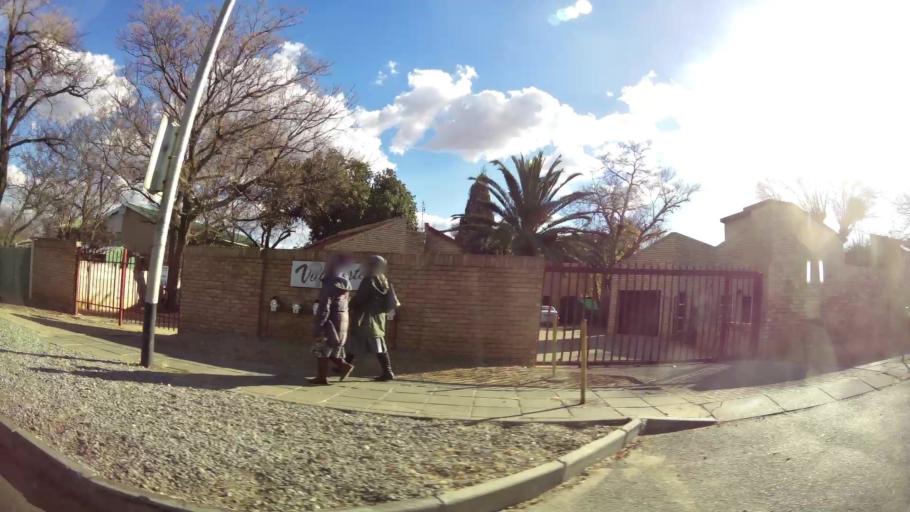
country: ZA
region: North-West
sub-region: Dr Kenneth Kaunda District Municipality
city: Klerksdorp
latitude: -26.8557
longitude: 26.6647
